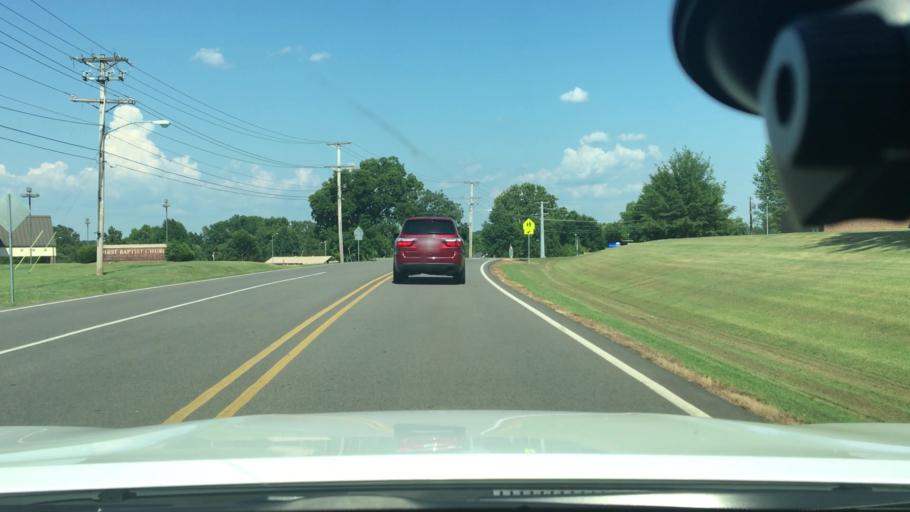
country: US
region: Arkansas
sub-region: Johnson County
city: Clarksville
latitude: 35.4616
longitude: -93.4832
